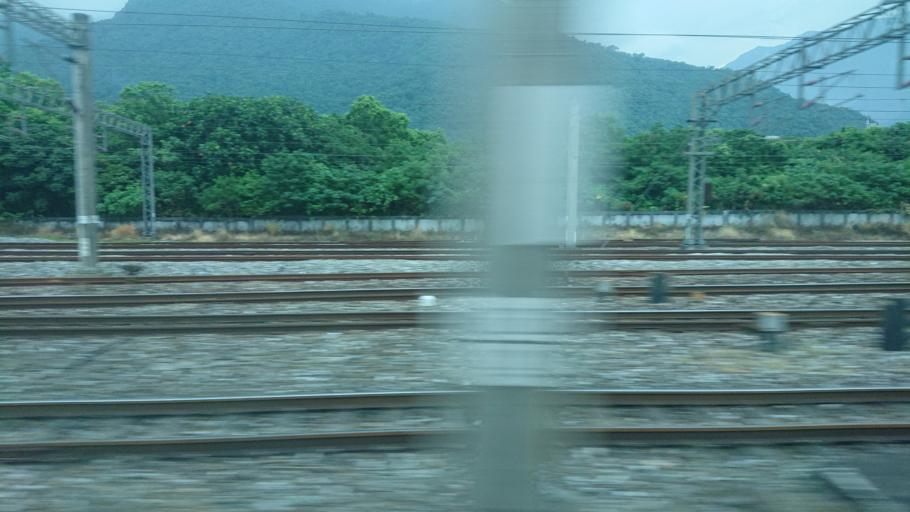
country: TW
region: Taiwan
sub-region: Hualien
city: Hualian
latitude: 24.1268
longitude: 121.6399
